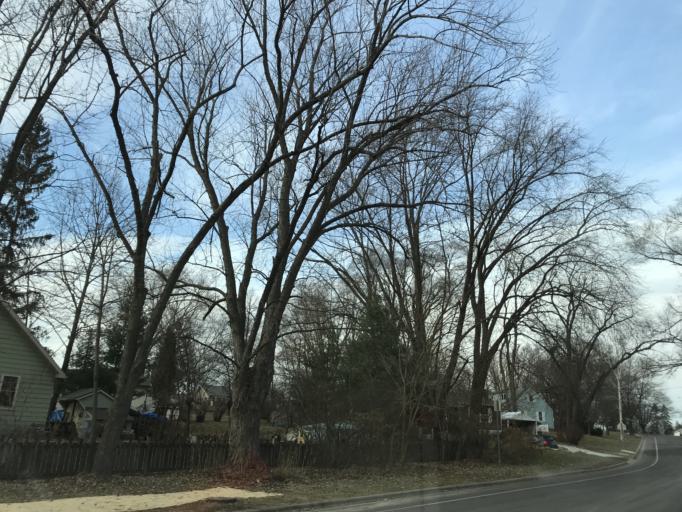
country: US
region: Wisconsin
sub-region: Dane County
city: Monona
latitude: 43.0625
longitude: -89.3379
